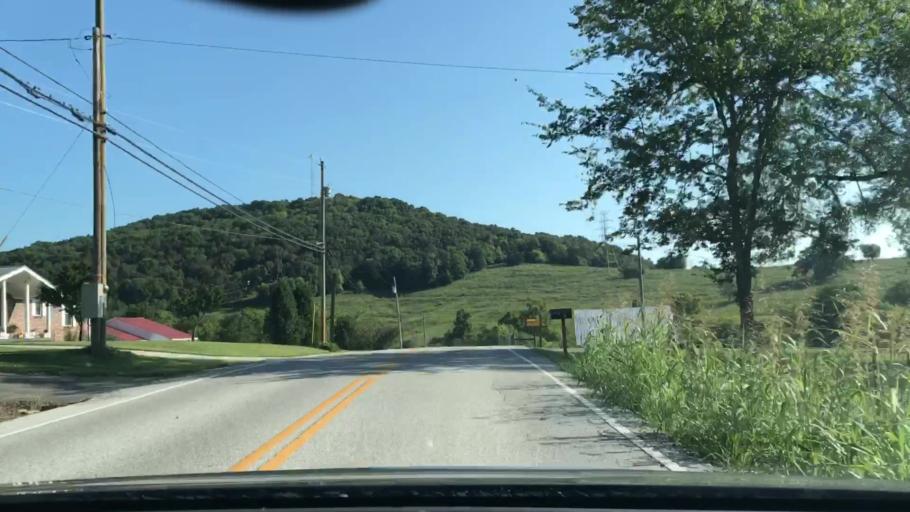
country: US
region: Tennessee
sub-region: Smith County
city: Carthage
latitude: 36.2793
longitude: -85.9480
